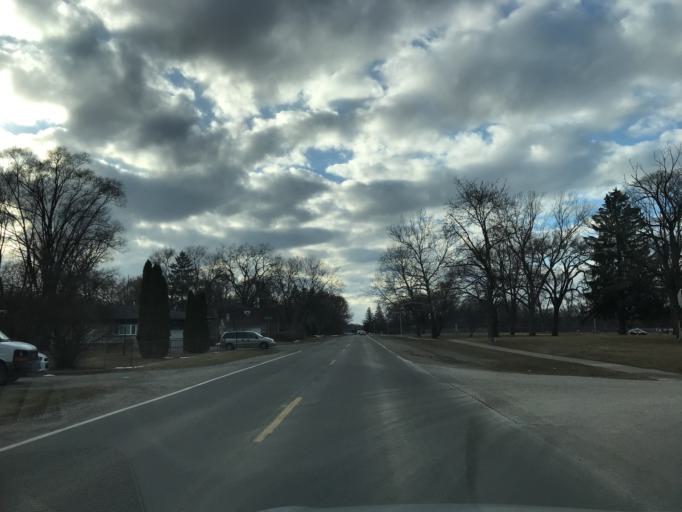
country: US
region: Michigan
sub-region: Oakland County
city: Farmington
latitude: 42.4529
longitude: -83.3291
